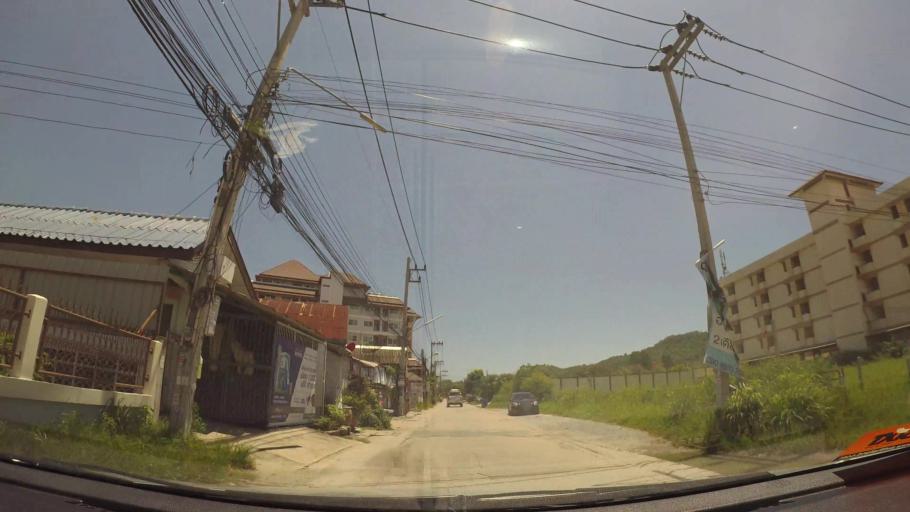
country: TH
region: Chon Buri
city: Si Racha
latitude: 13.1130
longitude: 100.9300
